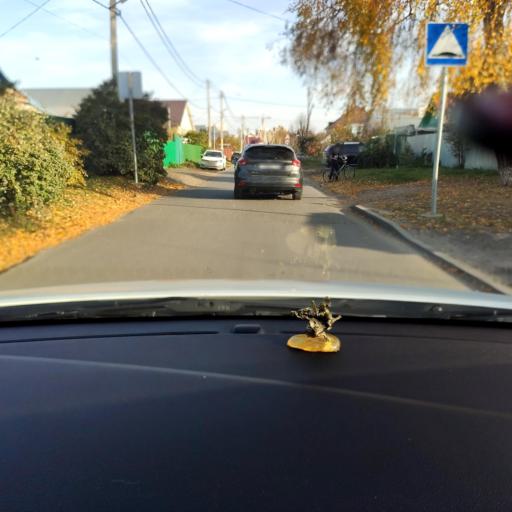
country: RU
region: Tatarstan
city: Osinovo
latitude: 55.8484
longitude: 48.8887
